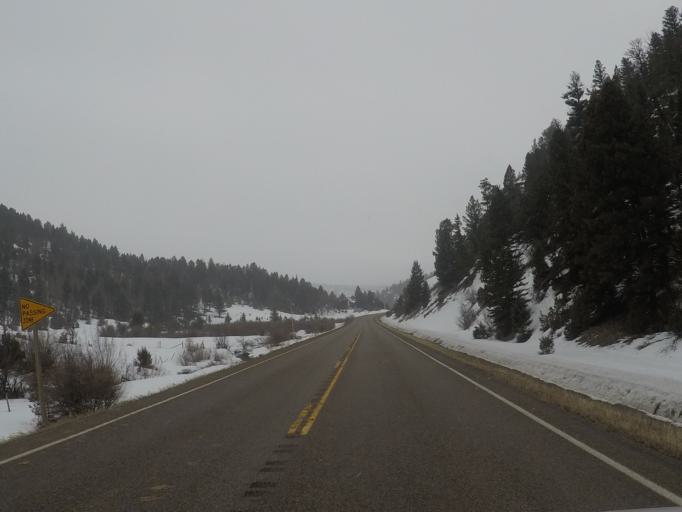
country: US
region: Montana
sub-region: Meagher County
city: White Sulphur Springs
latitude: 46.6831
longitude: -110.8751
